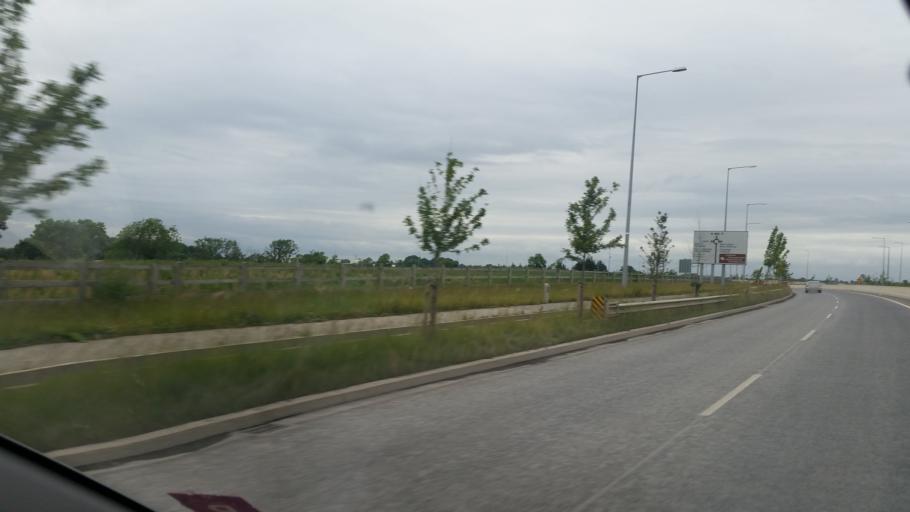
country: IE
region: Leinster
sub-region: Fingal County
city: Blanchardstown
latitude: 53.4222
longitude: -6.3667
